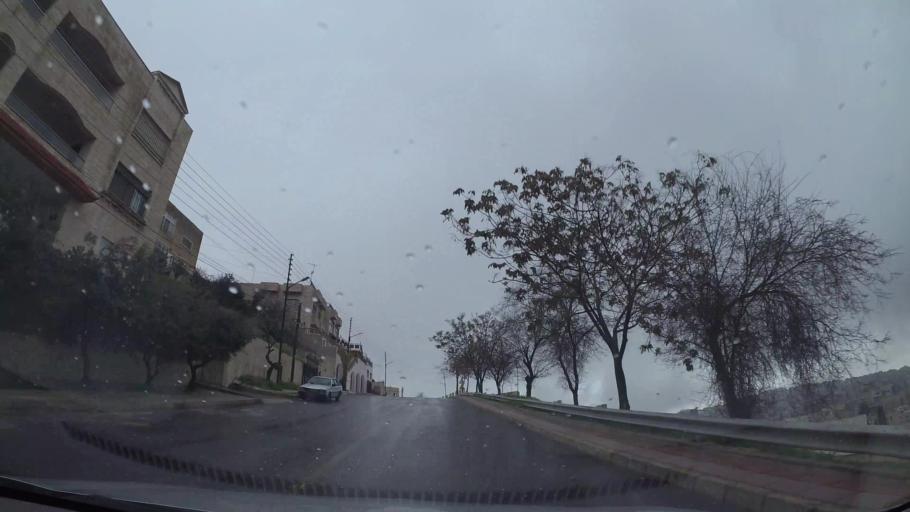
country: JO
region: Amman
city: Al Jubayhah
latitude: 32.0188
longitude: 35.8412
